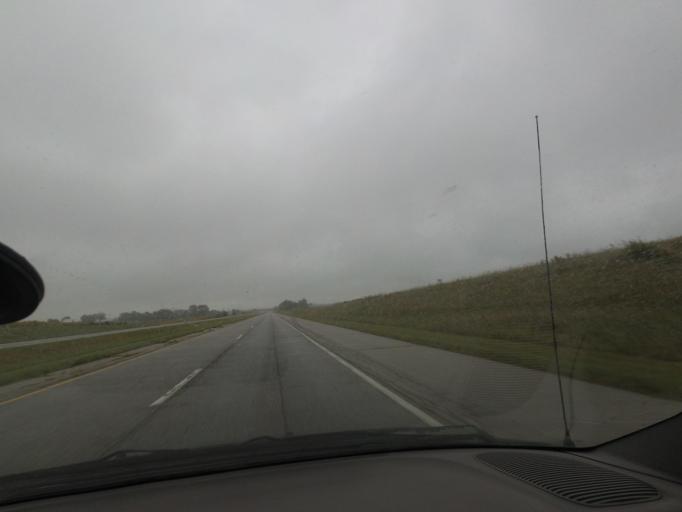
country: US
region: Illinois
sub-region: Pike County
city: Barry
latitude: 39.6978
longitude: -91.0154
